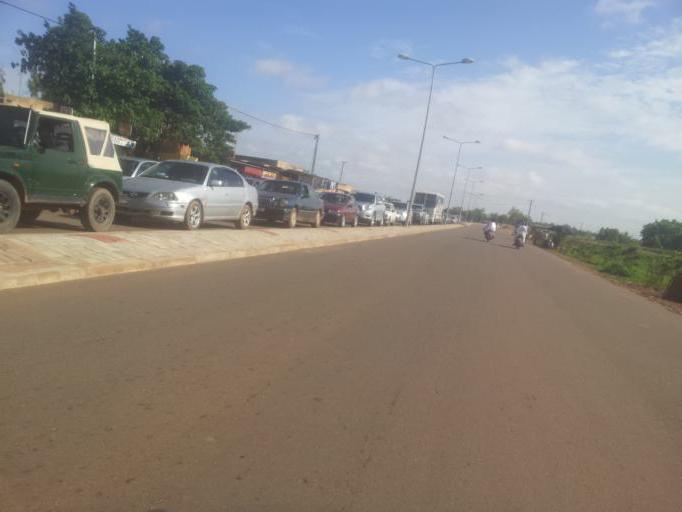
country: BF
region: Centre
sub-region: Kadiogo Province
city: Ouagadougou
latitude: 12.3779
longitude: -1.5699
